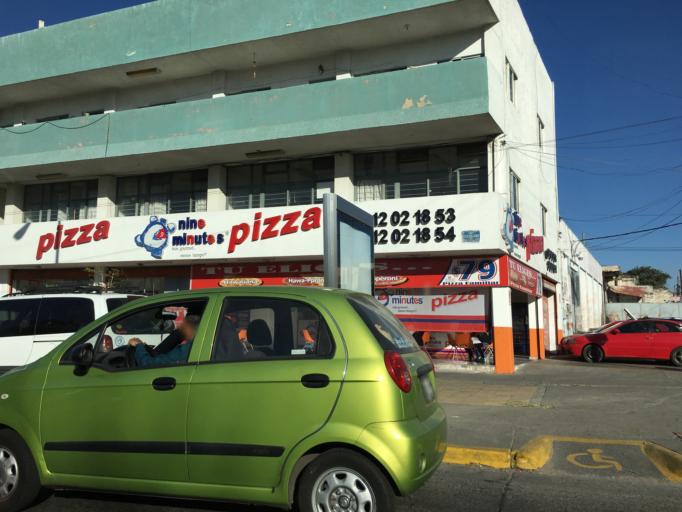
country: MX
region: Jalisco
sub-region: Zapopan
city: Zapopan
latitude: 20.7005
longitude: -103.3548
